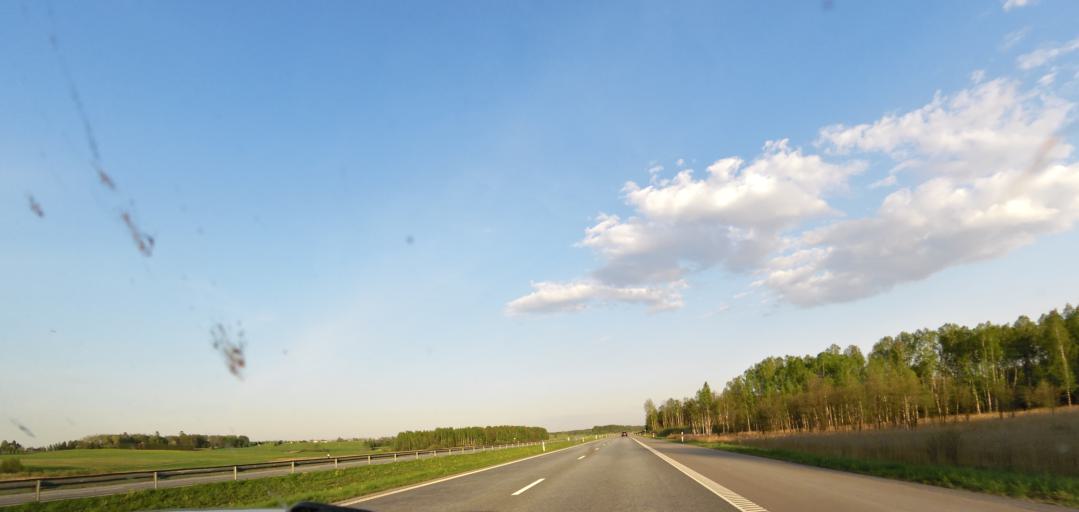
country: LT
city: Sirvintos
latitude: 54.9090
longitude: 25.0179
